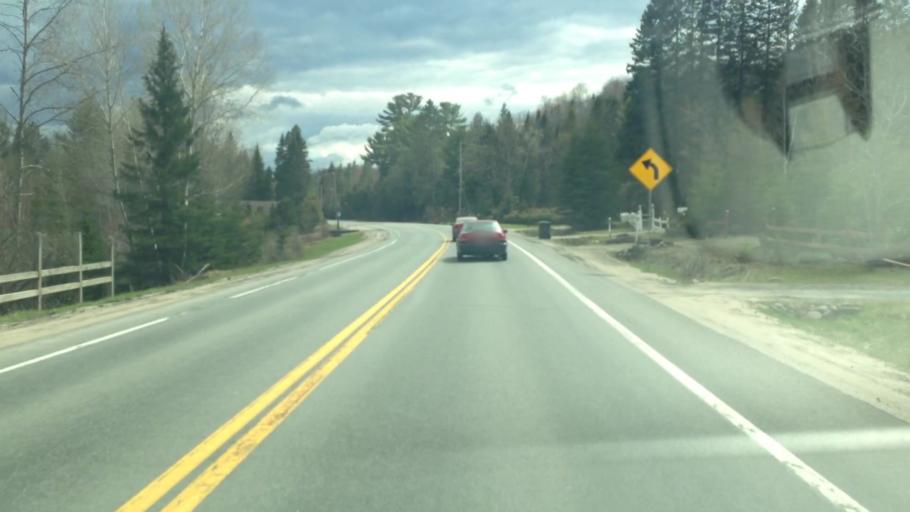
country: CA
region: Quebec
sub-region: Laurentides
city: Sainte-Adele
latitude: 46.0115
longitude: -74.1047
